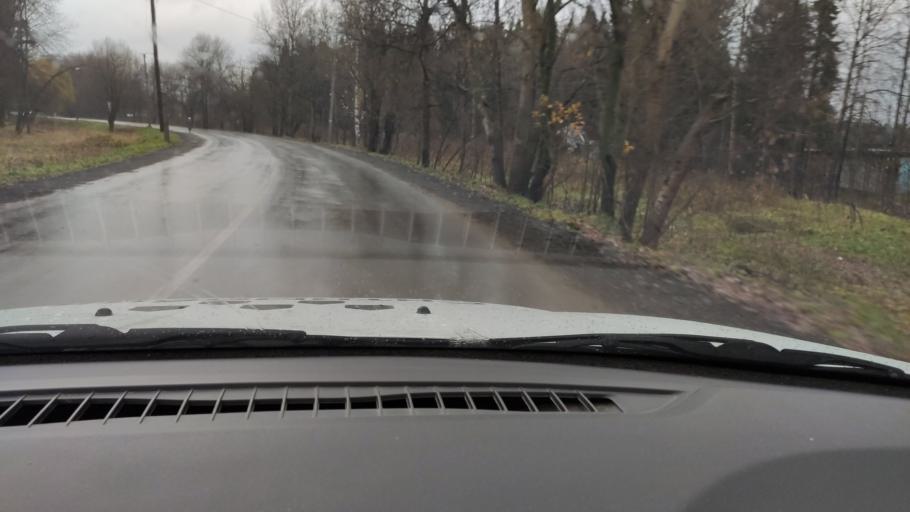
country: RU
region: Perm
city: Sylva
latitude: 58.0314
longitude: 56.7410
